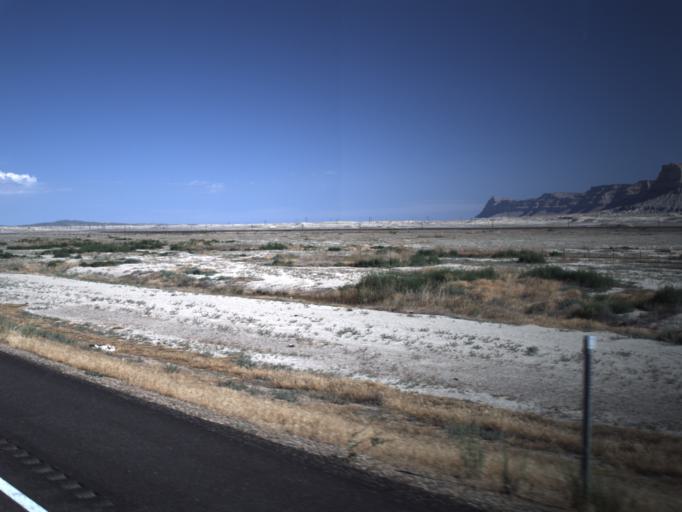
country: US
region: Utah
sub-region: Carbon County
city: East Carbon City
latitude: 38.9953
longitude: -110.2578
